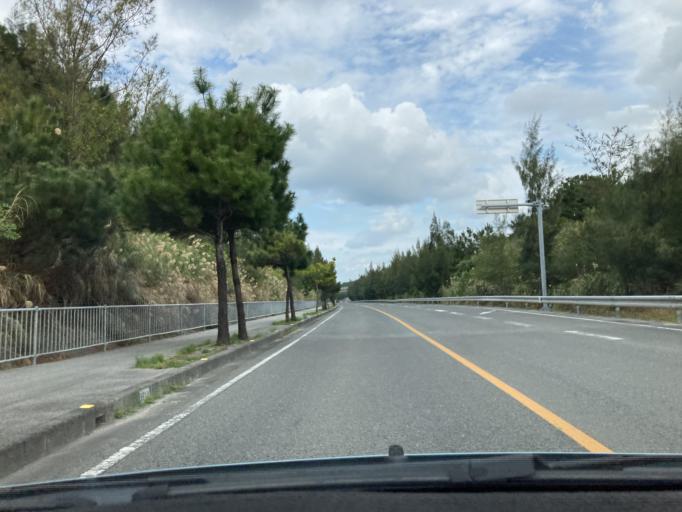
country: JP
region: Okinawa
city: Ishikawa
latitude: 26.4533
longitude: 127.8206
